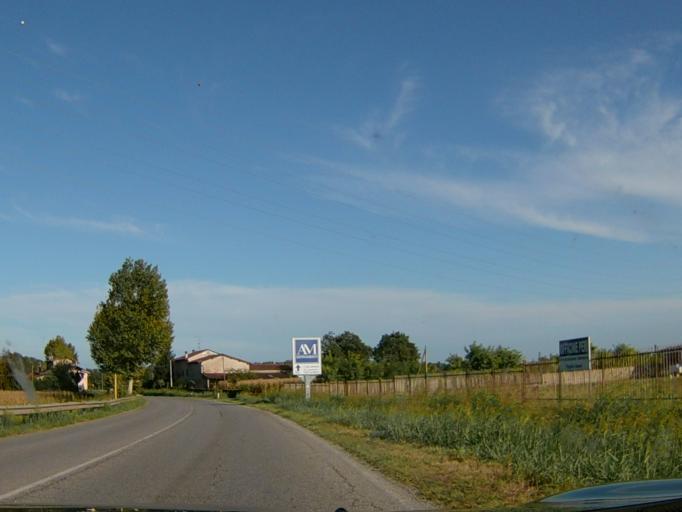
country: IT
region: Lombardy
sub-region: Provincia di Brescia
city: Ponte San Marco
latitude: 45.4758
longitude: 10.3979
